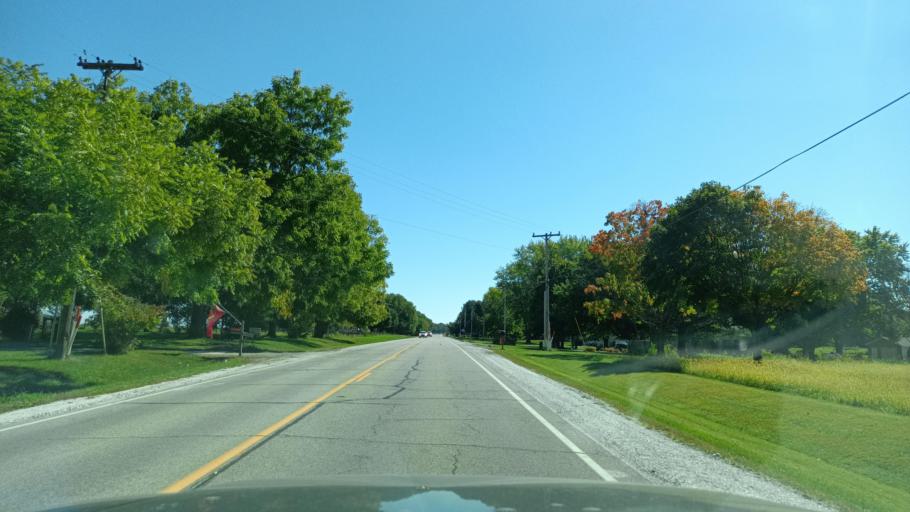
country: US
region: Illinois
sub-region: Peoria County
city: Hanna City
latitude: 40.7937
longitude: -89.7734
